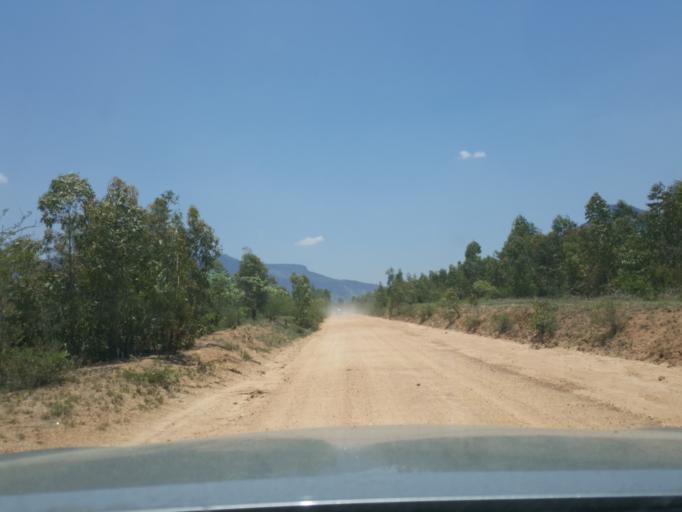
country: ZA
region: Limpopo
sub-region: Mopani District Municipality
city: Hoedspruit
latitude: -24.5864
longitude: 30.9719
